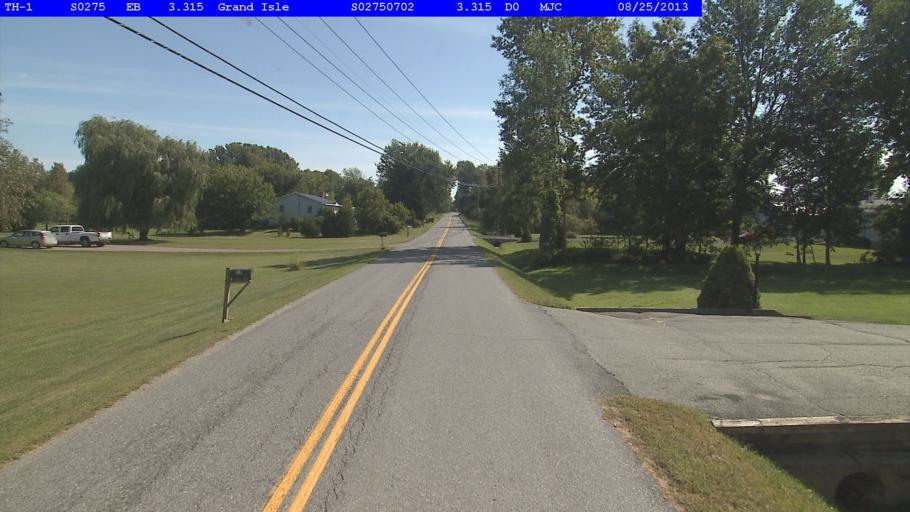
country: US
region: Vermont
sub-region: Grand Isle County
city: North Hero
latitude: 44.7351
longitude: -73.3147
